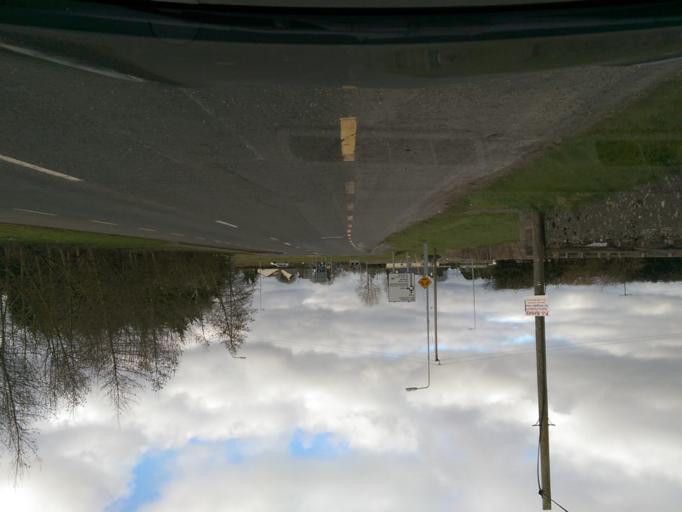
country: IE
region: Connaught
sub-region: County Galway
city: Ballinasloe
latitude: 53.3283
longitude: -8.1770
